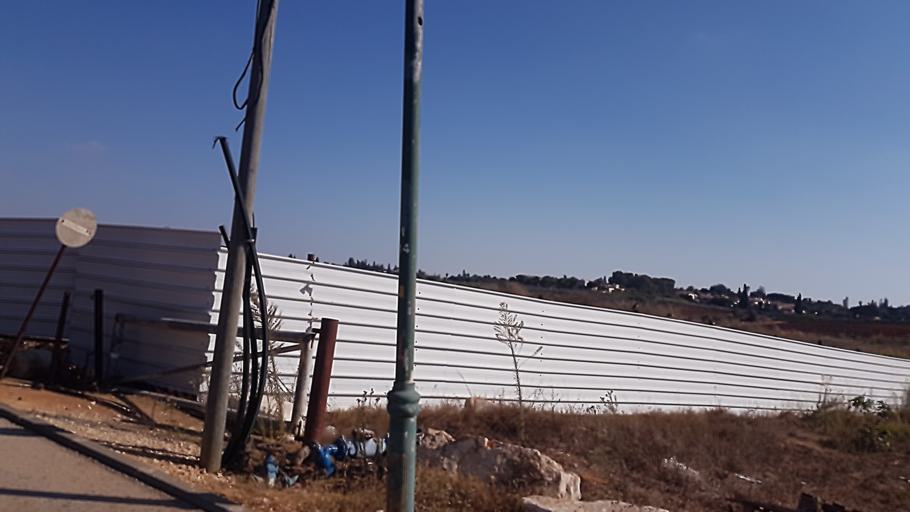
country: IL
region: Central District
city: Kfar Saba
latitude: 32.2029
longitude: 34.9068
